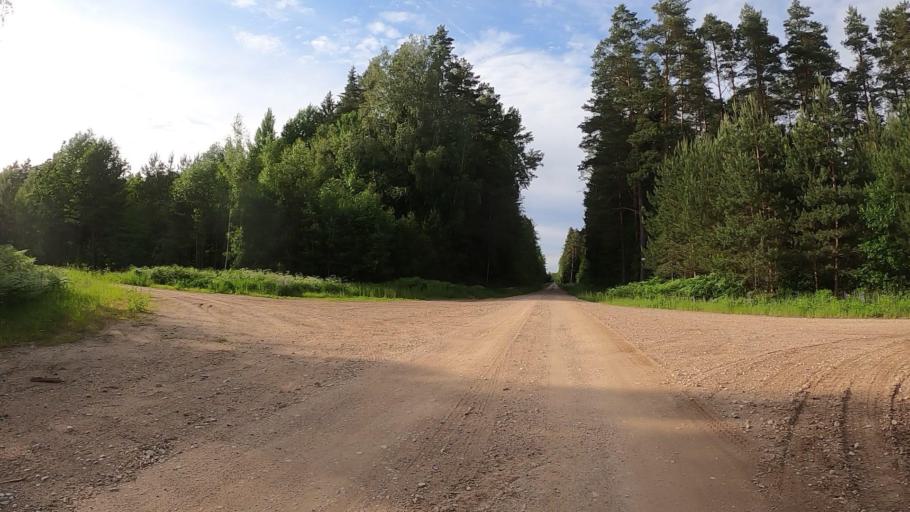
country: LV
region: Ozolnieku
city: Ozolnieki
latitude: 56.7589
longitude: 23.7916
